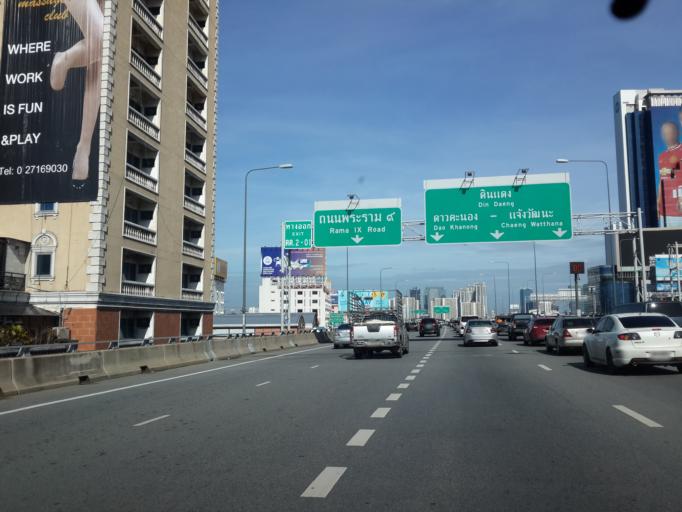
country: TH
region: Bangkok
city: Watthana
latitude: 13.7528
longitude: 100.5888
